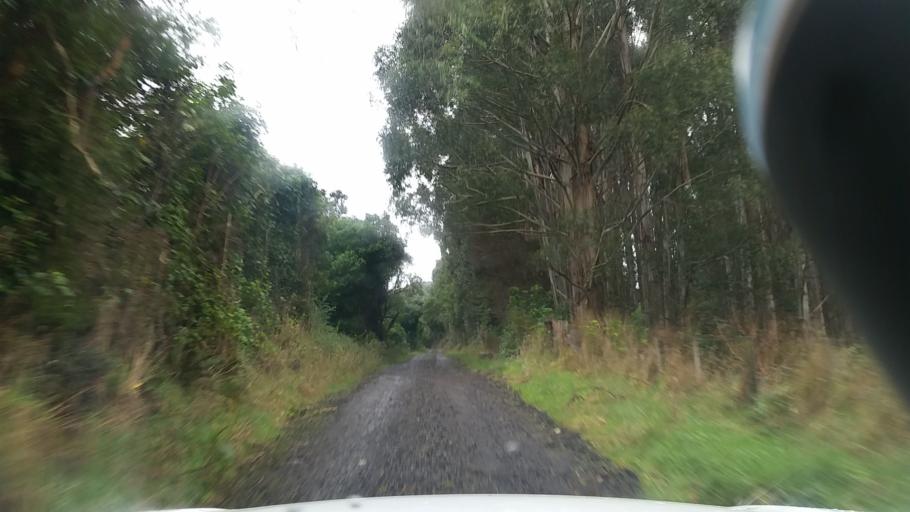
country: NZ
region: Canterbury
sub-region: Christchurch City
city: Christchurch
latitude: -43.7555
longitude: 173.0418
